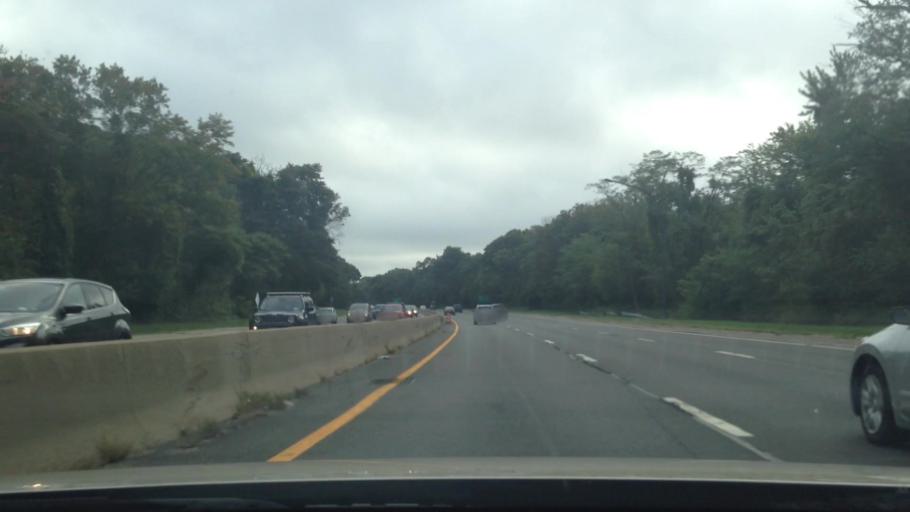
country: US
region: New York
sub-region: Suffolk County
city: North Babylon
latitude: 40.7323
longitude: -73.3318
